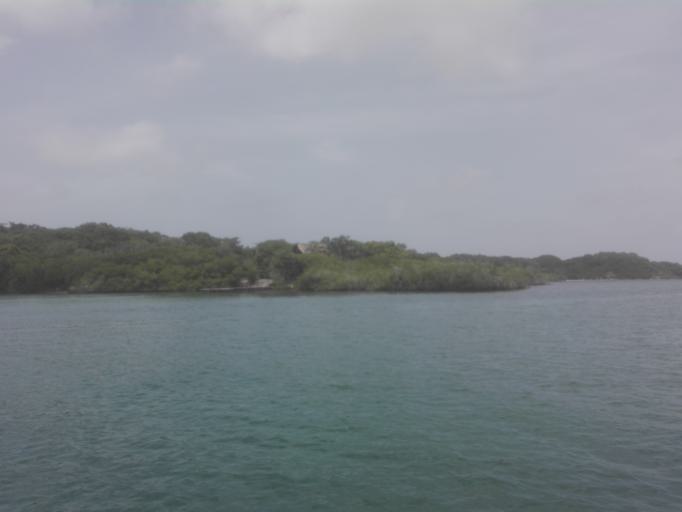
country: CO
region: Bolivar
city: Turbana
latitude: 10.1603
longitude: -75.6747
